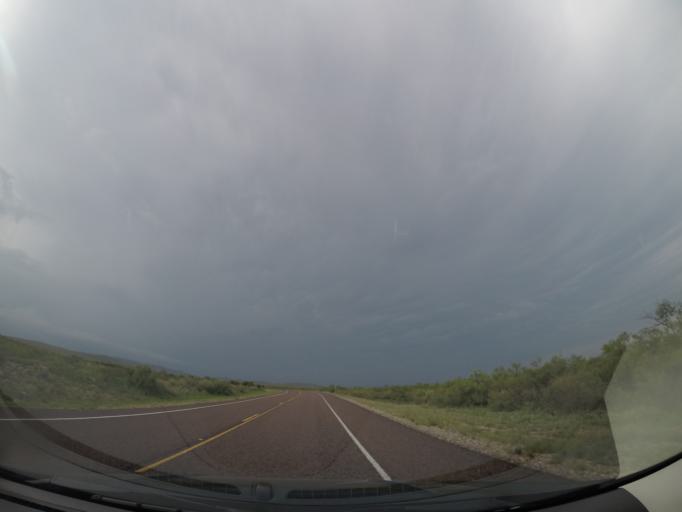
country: US
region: Texas
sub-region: Brewster County
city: Alpine
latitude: 30.0034
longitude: -103.2710
